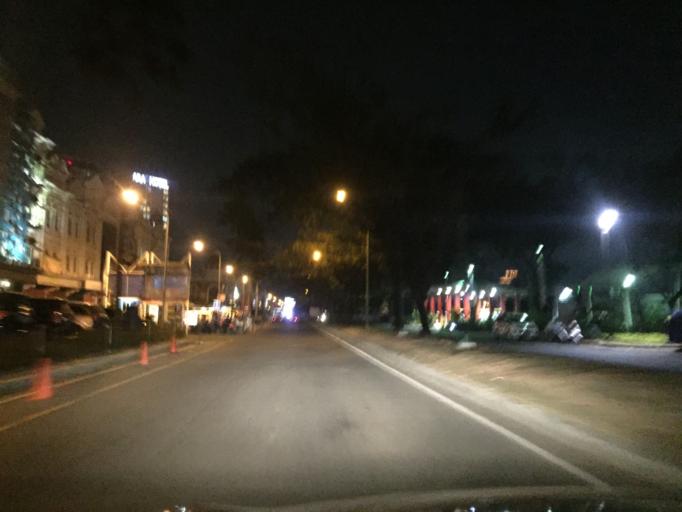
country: ID
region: Banten
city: Tangerang
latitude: -6.2433
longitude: 106.6280
